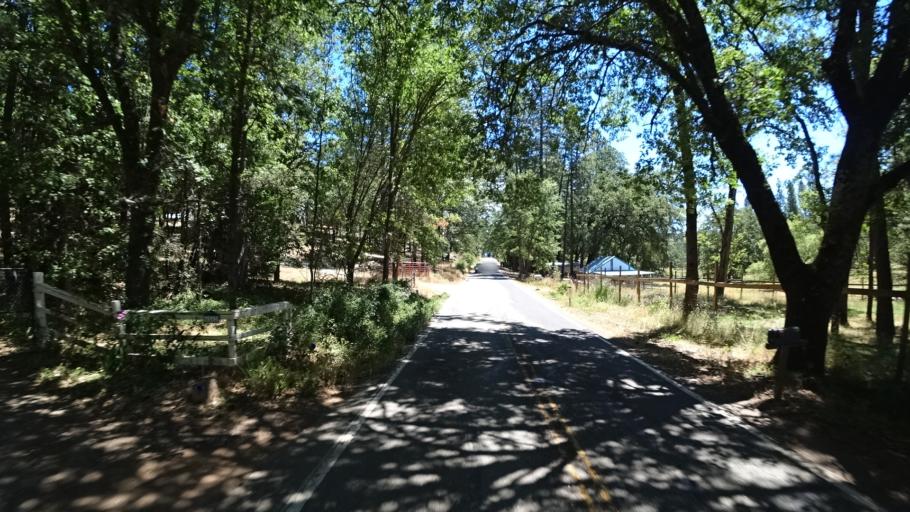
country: US
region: California
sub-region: Amador County
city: Pioneer
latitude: 38.3465
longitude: -120.5675
